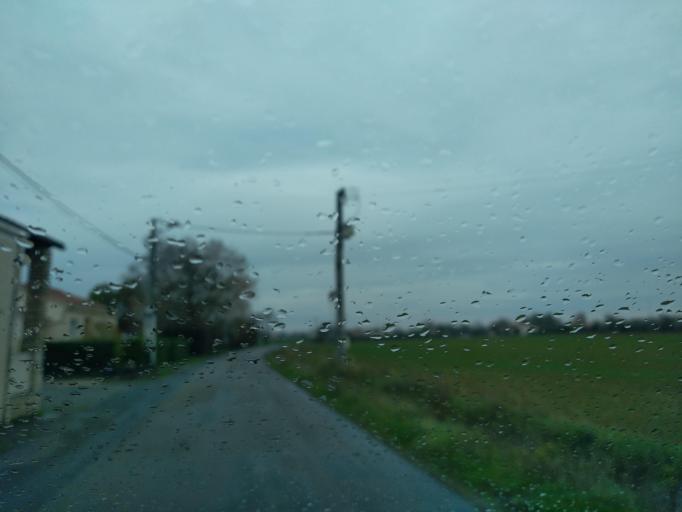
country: FR
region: Pays de la Loire
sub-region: Departement de la Vendee
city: Maillezais
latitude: 46.3674
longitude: -0.7322
